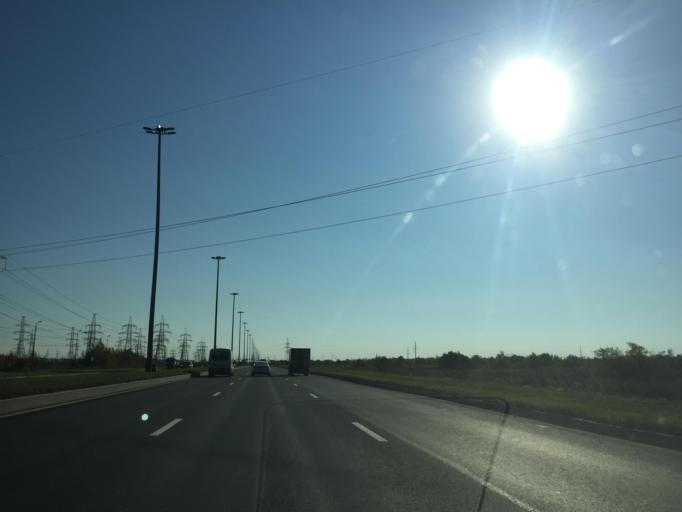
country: RU
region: St.-Petersburg
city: Petro-Slavyanka
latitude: 59.7584
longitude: 30.5150
